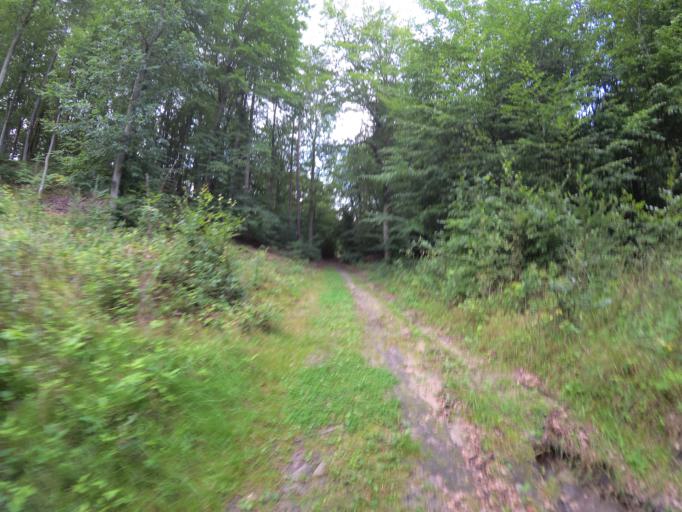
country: PL
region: Pomeranian Voivodeship
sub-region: Gdynia
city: Wielki Kack
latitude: 54.5056
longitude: 18.4393
